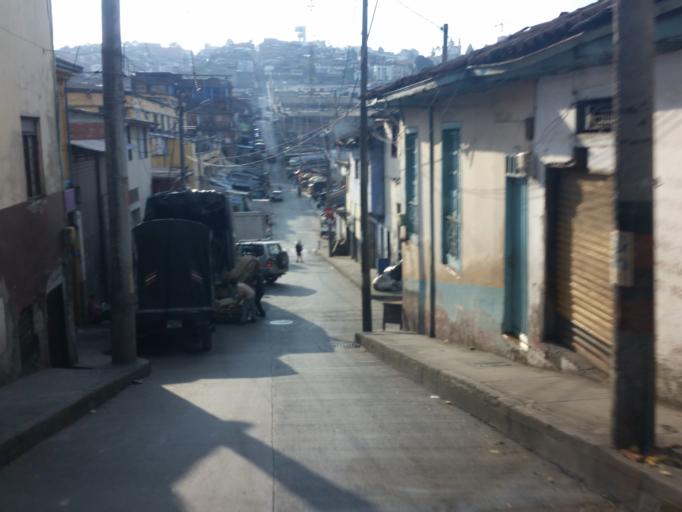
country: CO
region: Caldas
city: Manizales
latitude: 5.0724
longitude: -75.5160
